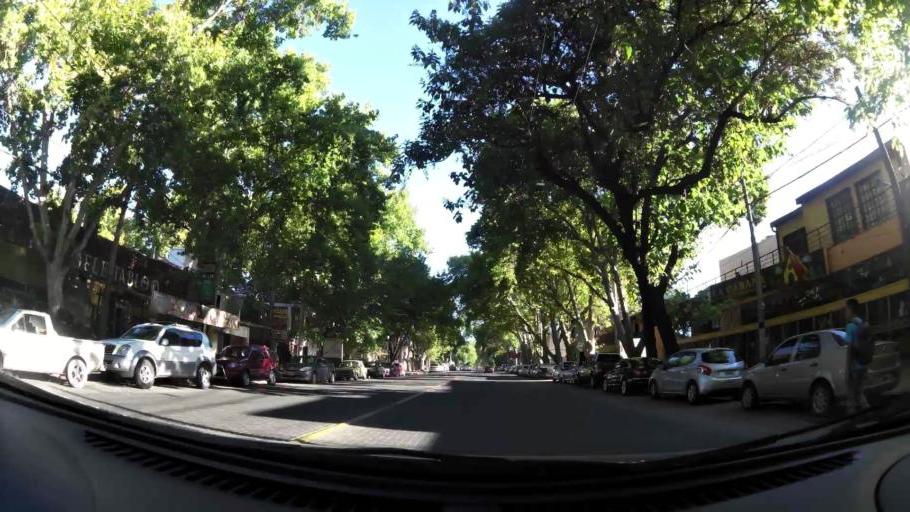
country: AR
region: Mendoza
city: Mendoza
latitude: -32.8722
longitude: -68.8346
